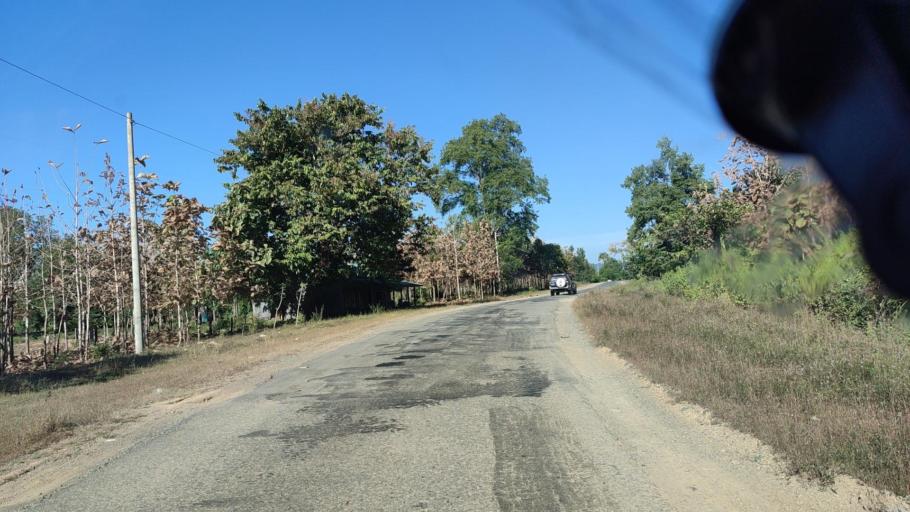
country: MM
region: Rakhine
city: Sittwe
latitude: 19.9443
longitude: 93.7449
